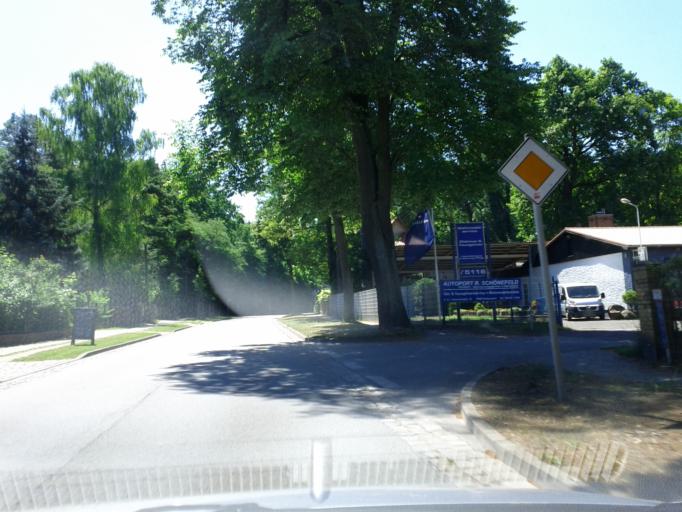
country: DE
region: Brandenburg
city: Woltersdorf
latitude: 52.4439
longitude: 13.7569
